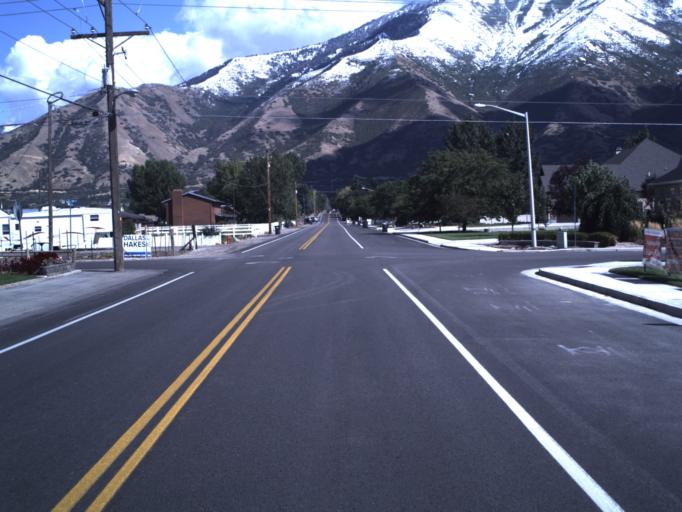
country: US
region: Utah
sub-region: Utah County
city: Mapleton
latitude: 40.1157
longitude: -111.5886
